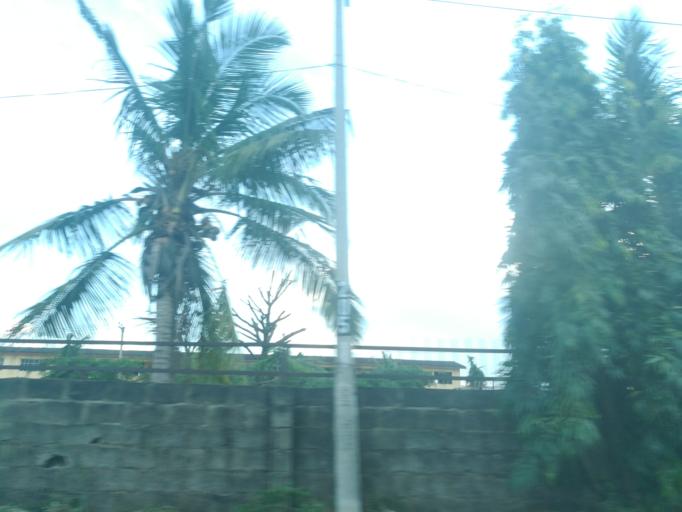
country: NG
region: Lagos
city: Ebute Ikorodu
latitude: 6.6229
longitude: 3.4812
